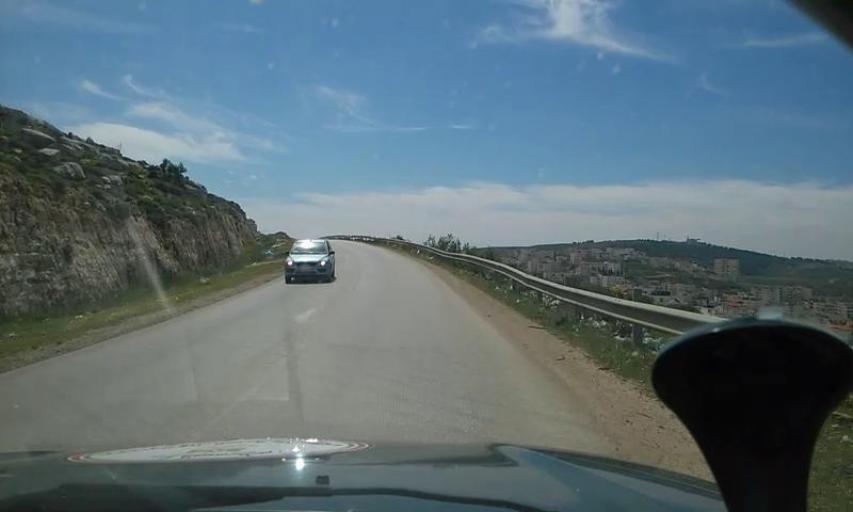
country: PS
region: West Bank
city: Al Judayrah
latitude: 31.8583
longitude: 35.2018
